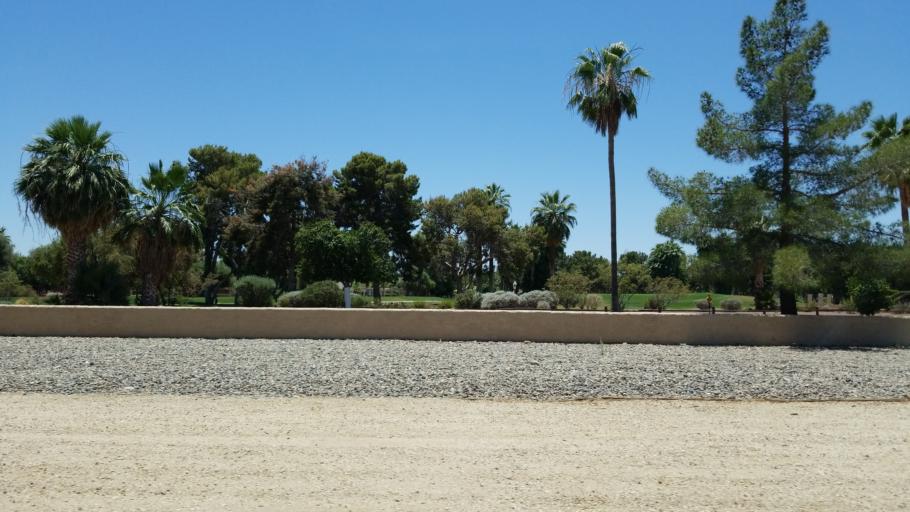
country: US
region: Arizona
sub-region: Maricopa County
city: Litchfield Park
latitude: 33.5079
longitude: -112.3450
